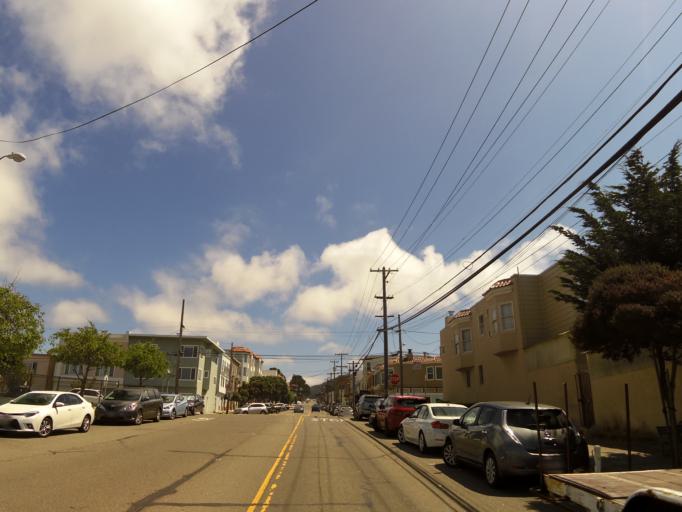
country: US
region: California
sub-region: San Mateo County
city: Daly City
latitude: 37.7391
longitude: -122.4813
